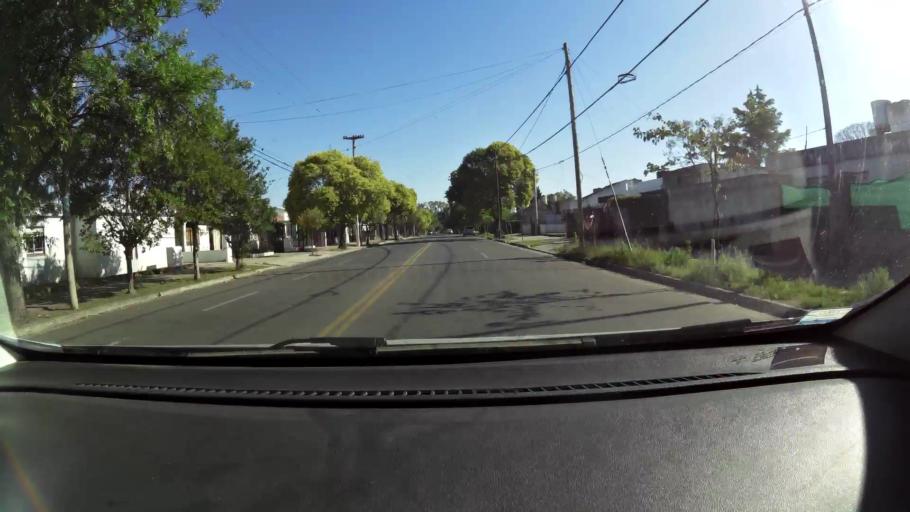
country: AR
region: Cordoba
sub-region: Departamento de Capital
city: Cordoba
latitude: -31.3645
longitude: -64.2125
